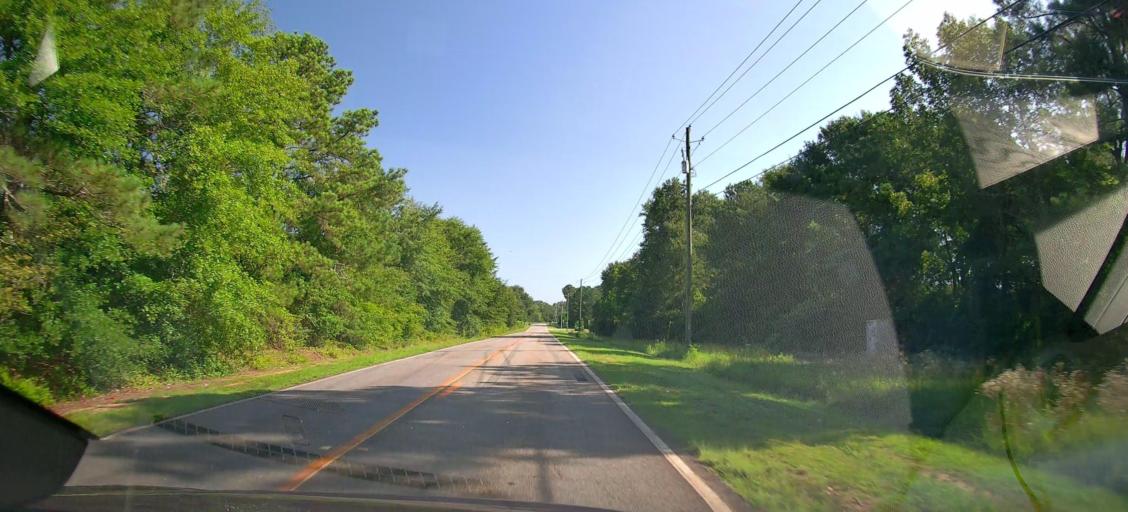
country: US
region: Georgia
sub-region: Peach County
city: Byron
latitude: 32.7223
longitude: -83.7096
